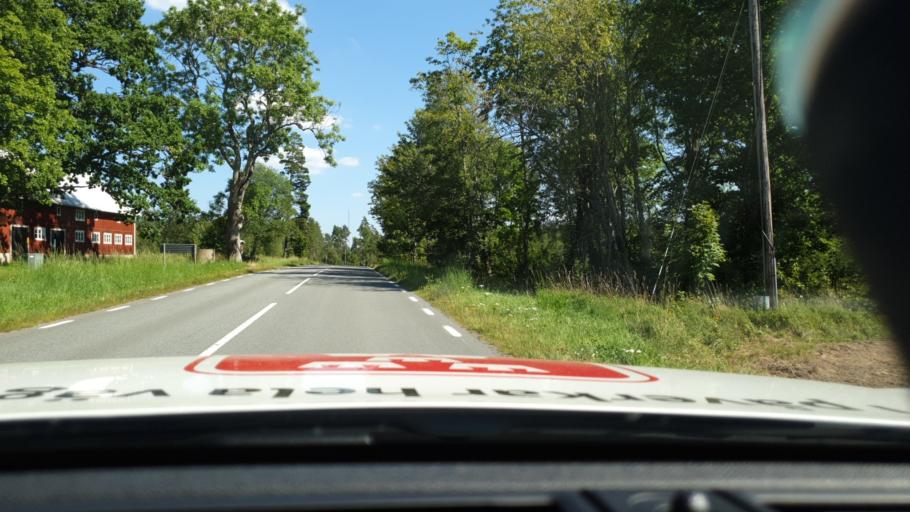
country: SE
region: Joenkoeping
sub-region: Aneby Kommun
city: Hestra
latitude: 57.8913
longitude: 14.5265
